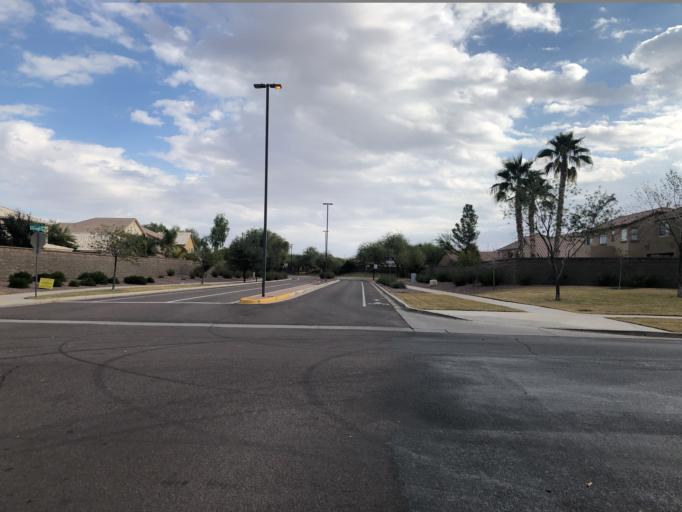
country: US
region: Arizona
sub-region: Maricopa County
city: Queen Creek
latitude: 33.2730
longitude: -111.7073
